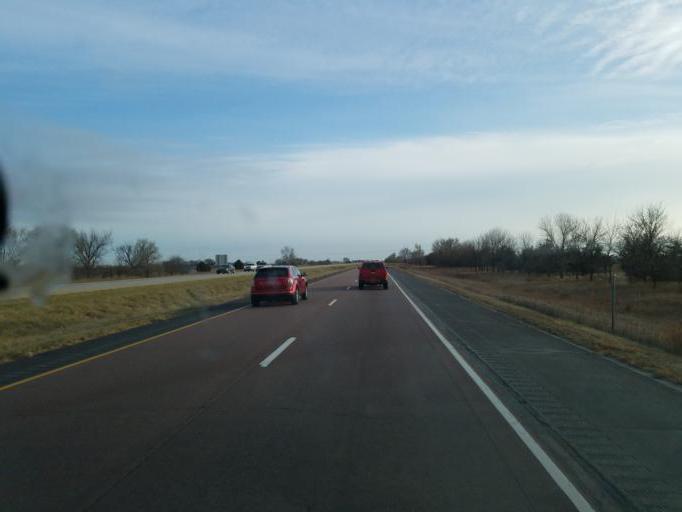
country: US
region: Iowa
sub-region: Woodbury County
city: Sergeant Bluff
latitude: 42.3659
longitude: -96.3471
